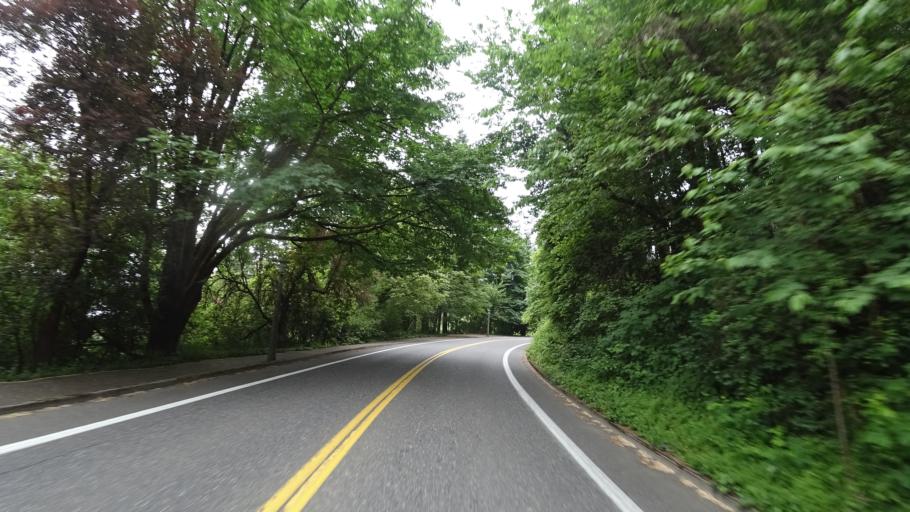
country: US
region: Oregon
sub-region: Multnomah County
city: Portland
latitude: 45.4925
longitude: -122.6815
